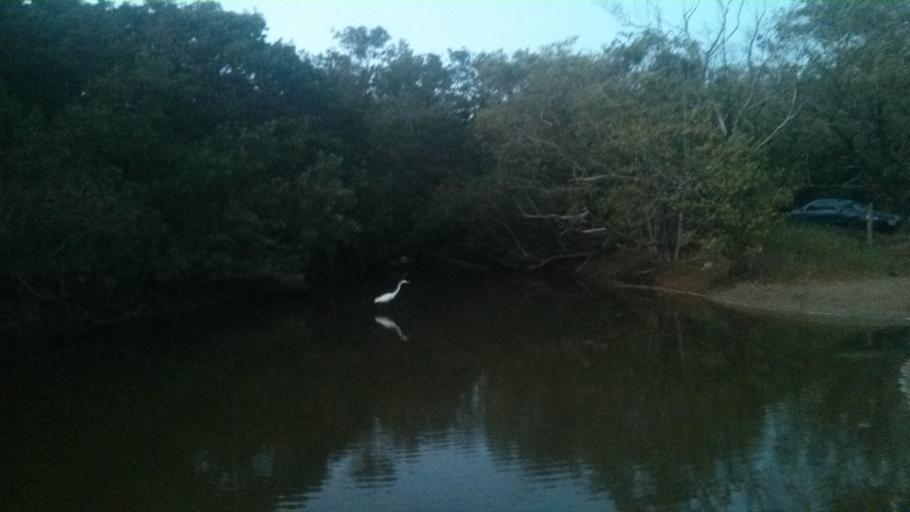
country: CR
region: Guanacaste
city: Sardinal
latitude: 10.3387
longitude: -85.8523
